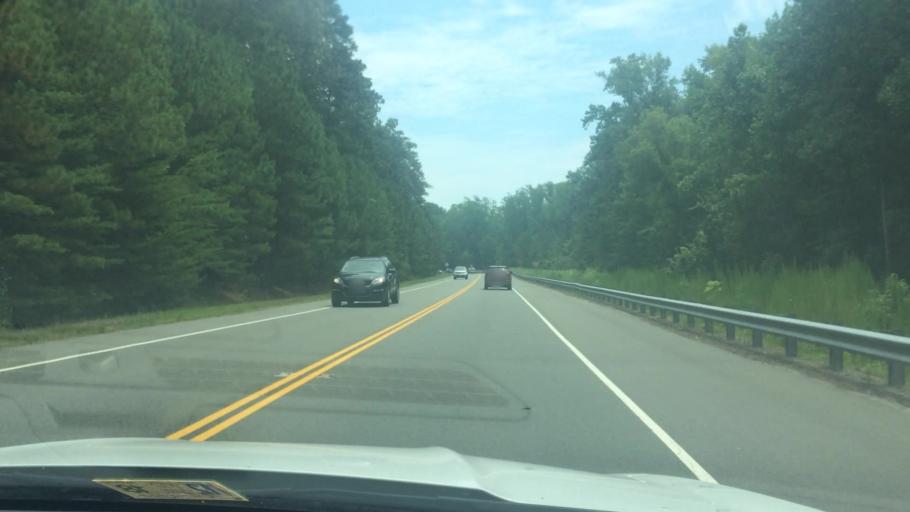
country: US
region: Virginia
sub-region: James City County
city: Williamsburg
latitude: 37.2668
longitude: -76.7713
